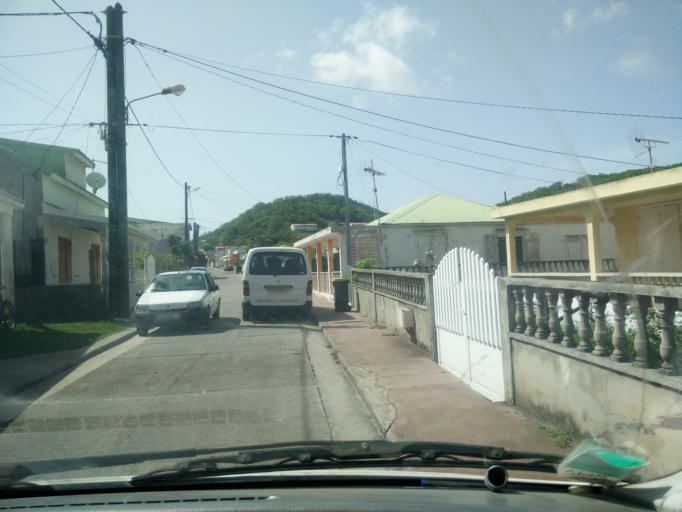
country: GP
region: Guadeloupe
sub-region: Guadeloupe
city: Terre-de-Bas
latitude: 15.8479
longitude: -61.6434
